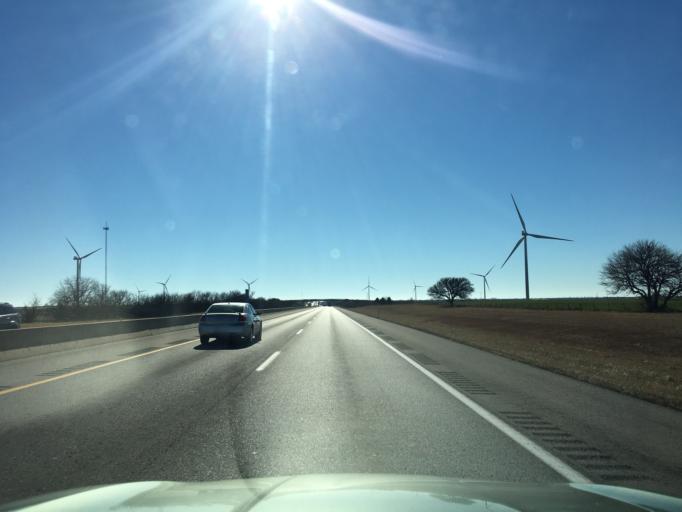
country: US
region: Kansas
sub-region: Sumner County
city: Wellington
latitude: 37.1500
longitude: -97.3395
